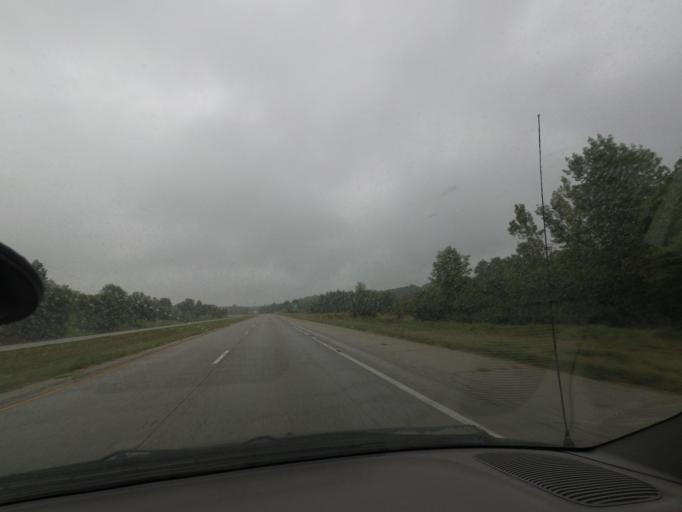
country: US
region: Illinois
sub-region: Pike County
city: Barry
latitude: 39.7137
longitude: -91.0626
